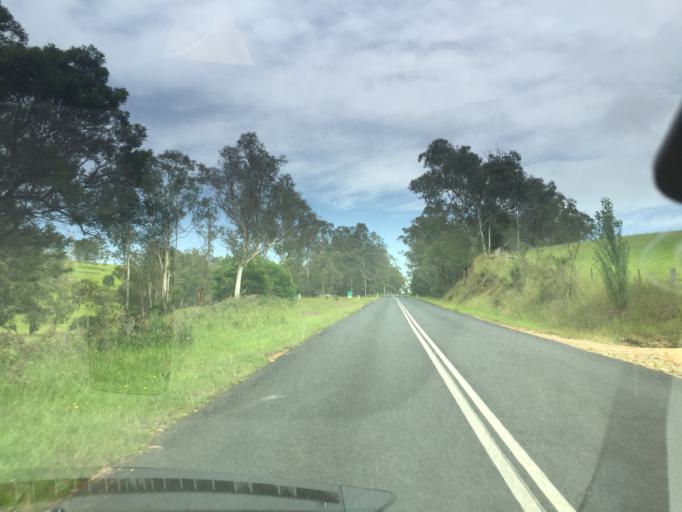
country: AU
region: New South Wales
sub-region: Bega Valley
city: Bega
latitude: -36.7103
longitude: 149.5955
